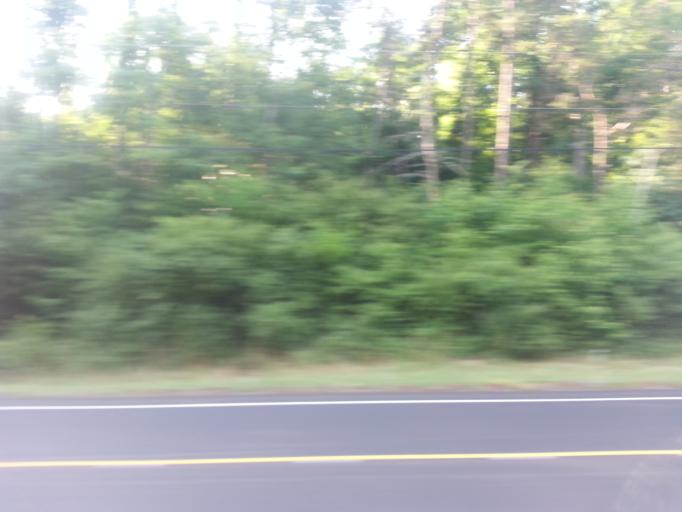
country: US
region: Tennessee
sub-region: Knox County
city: Knoxville
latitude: 35.8857
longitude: -83.9480
